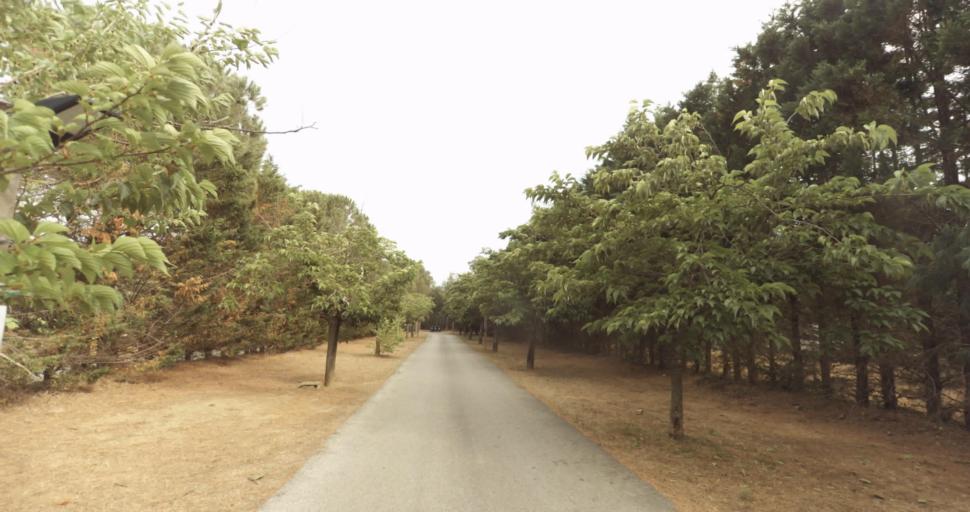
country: FR
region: Provence-Alpes-Cote d'Azur
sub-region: Departement du Var
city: Gassin
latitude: 43.2181
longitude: 6.5783
